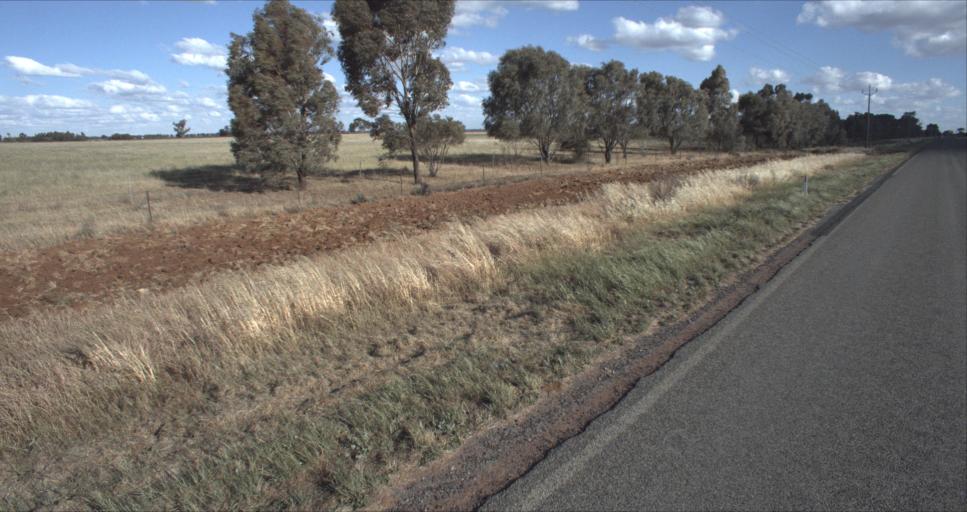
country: AU
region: New South Wales
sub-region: Leeton
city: Leeton
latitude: -34.5303
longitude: 146.2816
